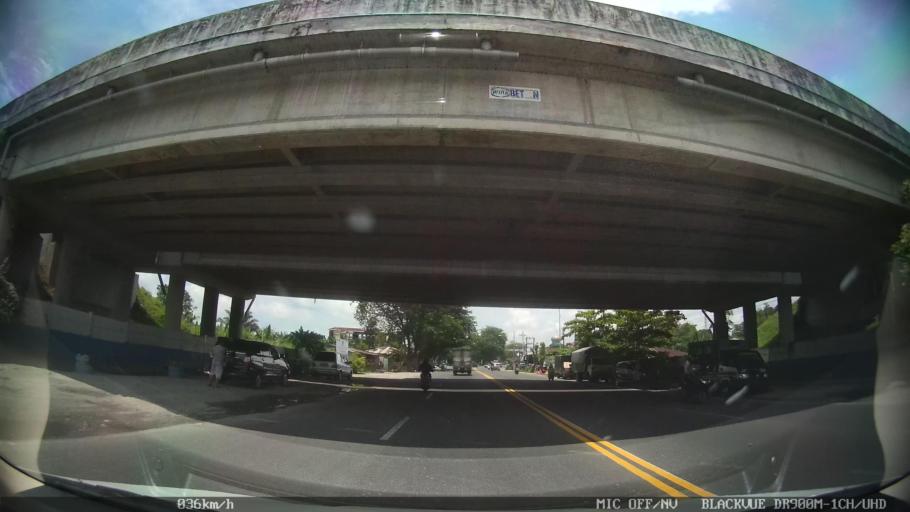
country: ID
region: North Sumatra
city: Percut
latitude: 3.5523
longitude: 98.8528
